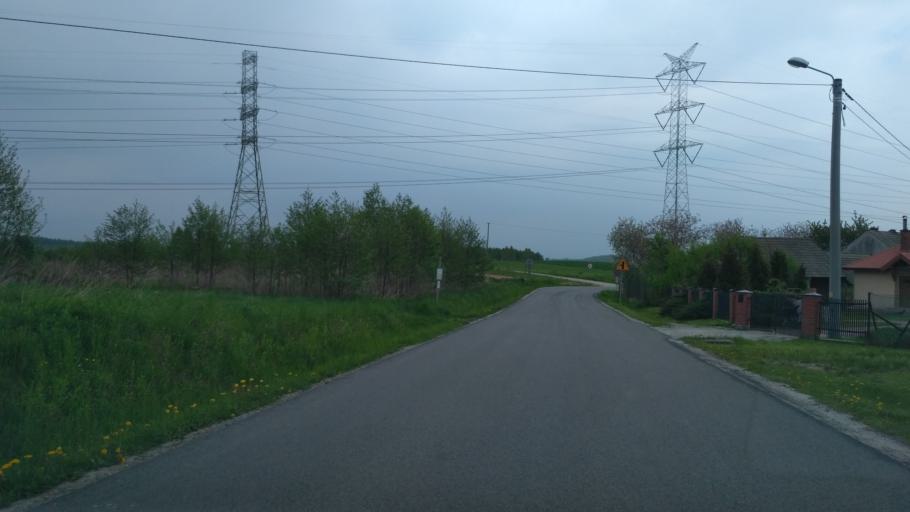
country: PL
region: Lesser Poland Voivodeship
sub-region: Powiat tarnowski
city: Tarnowiec
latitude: 49.9456
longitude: 21.0191
